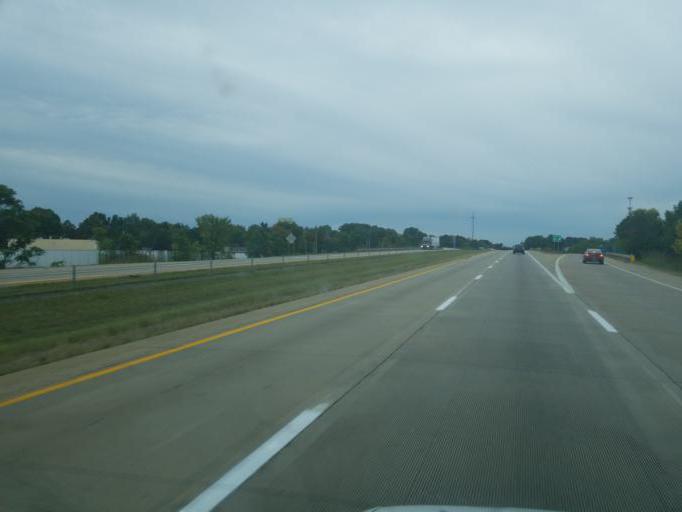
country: US
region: Ohio
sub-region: Portage County
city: Brimfield
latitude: 41.1025
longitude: -81.3749
